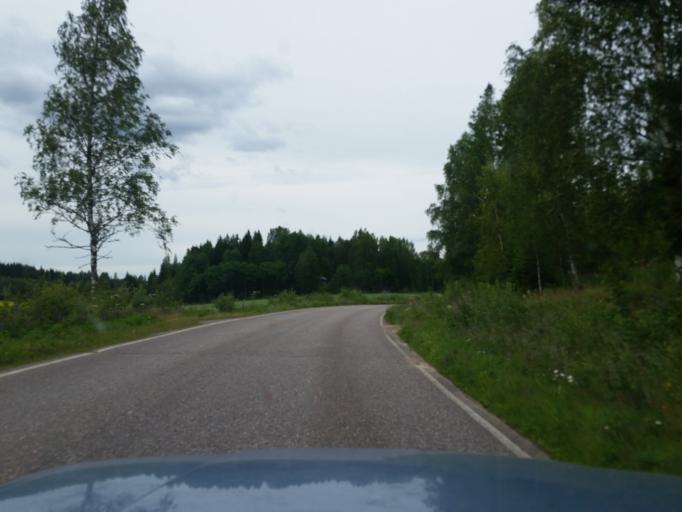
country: FI
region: Uusimaa
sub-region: Helsinki
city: Sammatti
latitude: 60.3993
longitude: 23.8158
